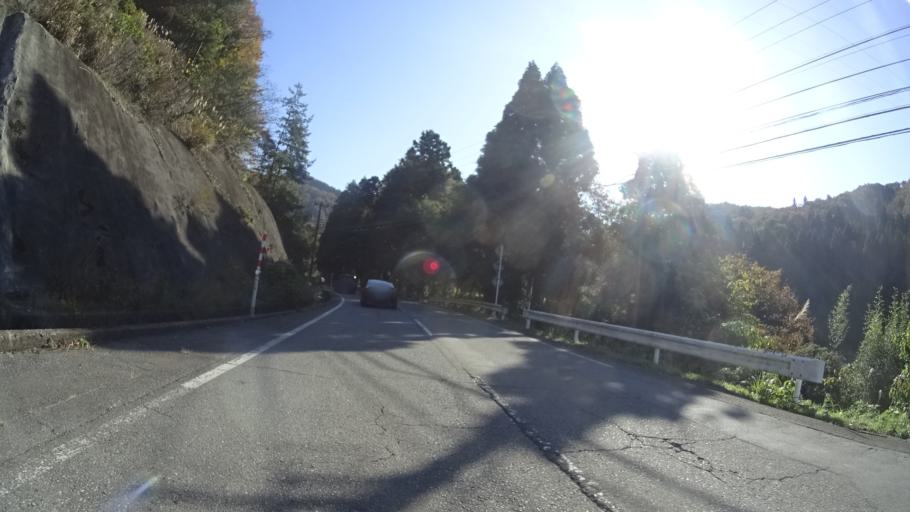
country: JP
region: Ishikawa
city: Komatsu
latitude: 36.3782
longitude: 136.5385
